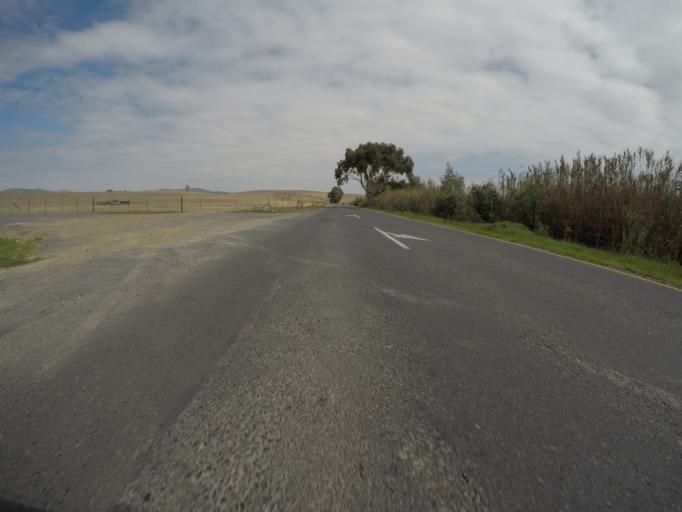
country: ZA
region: Western Cape
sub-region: City of Cape Town
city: Sunset Beach
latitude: -33.7853
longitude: 18.5554
